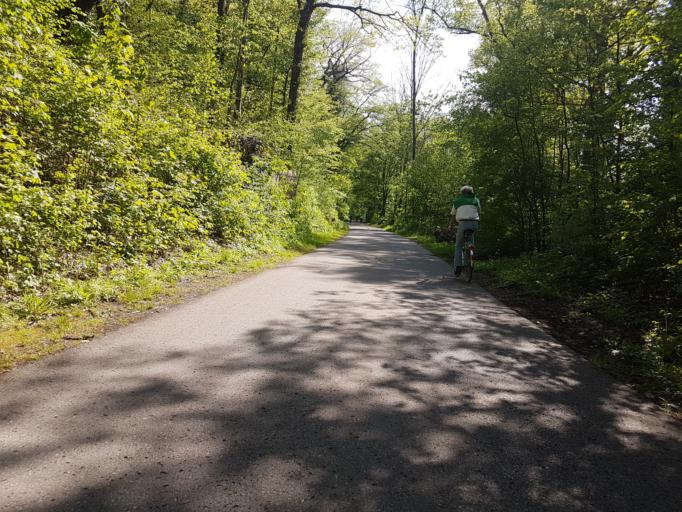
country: DE
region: Baden-Wuerttemberg
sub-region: Regierungsbezirk Stuttgart
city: Besigheim
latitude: 48.9724
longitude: 9.1485
